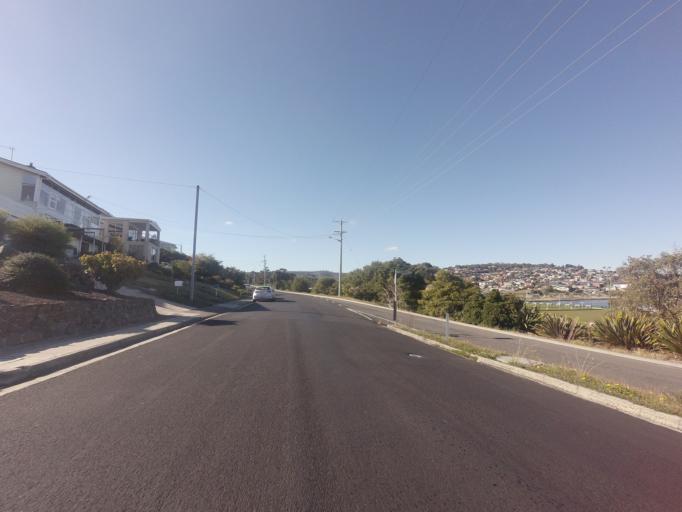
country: AU
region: Tasmania
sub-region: Clarence
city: Bellerive
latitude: -42.8707
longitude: 147.3626
